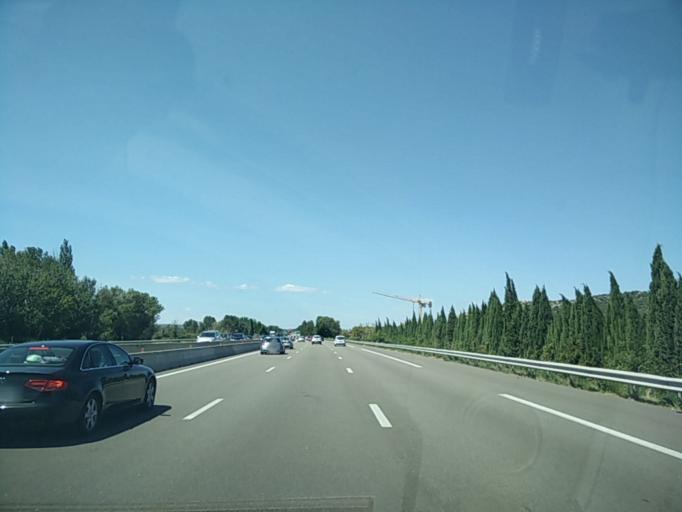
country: FR
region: Provence-Alpes-Cote d'Azur
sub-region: Departement du Vaucluse
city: Mornas
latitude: 44.1926
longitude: 4.7403
